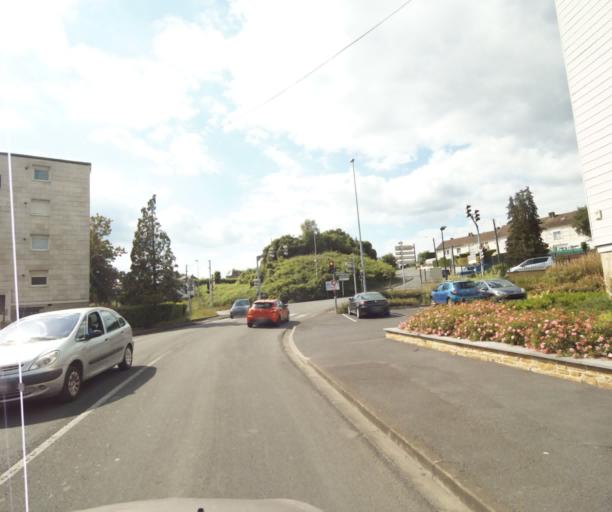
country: FR
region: Champagne-Ardenne
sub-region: Departement des Ardennes
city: Charleville-Mezieres
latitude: 49.7589
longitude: 4.7291
